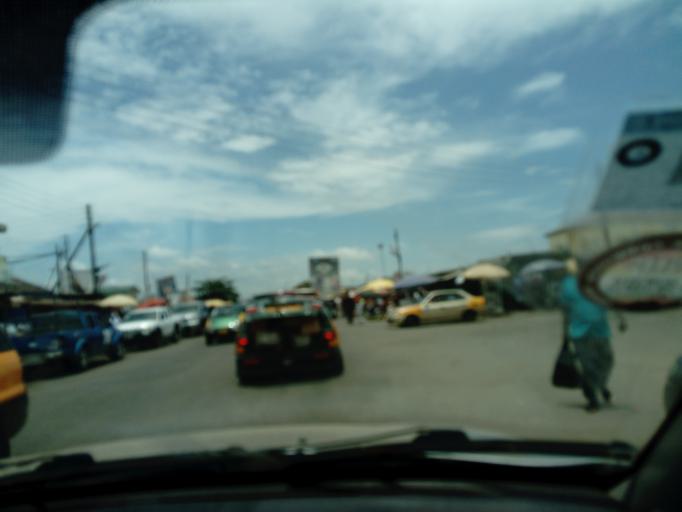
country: GH
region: Central
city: Cape Coast
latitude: 5.1321
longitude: -1.2757
